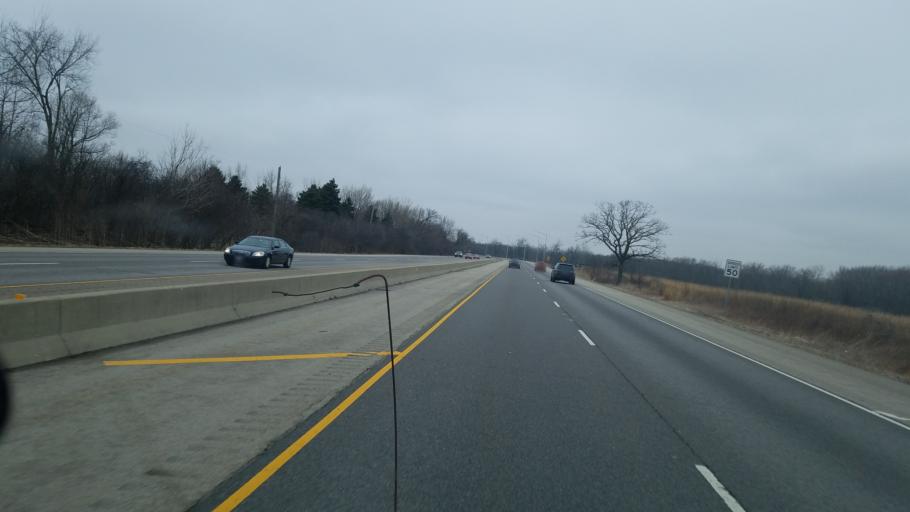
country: US
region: Illinois
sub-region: Lake County
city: Wadsworth
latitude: 42.4391
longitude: -87.9380
